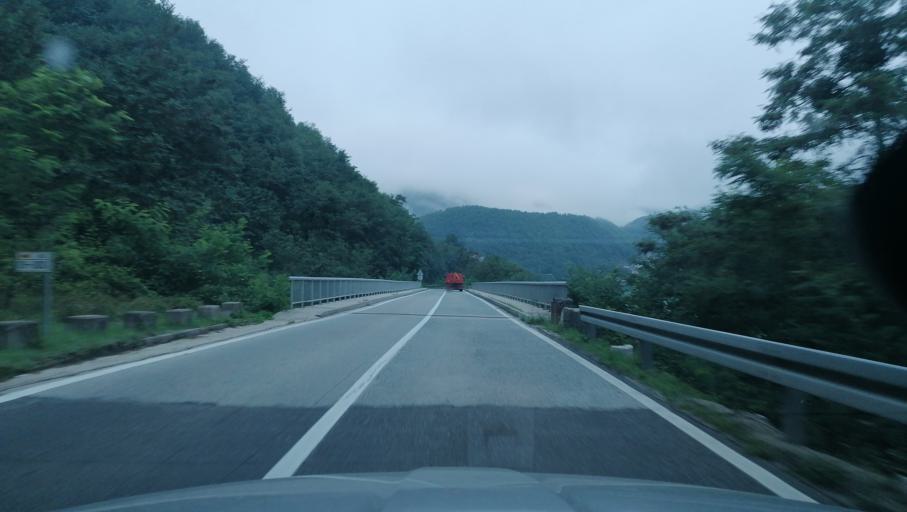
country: BA
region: Federation of Bosnia and Herzegovina
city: Jablanica
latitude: 43.7179
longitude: 17.7108
